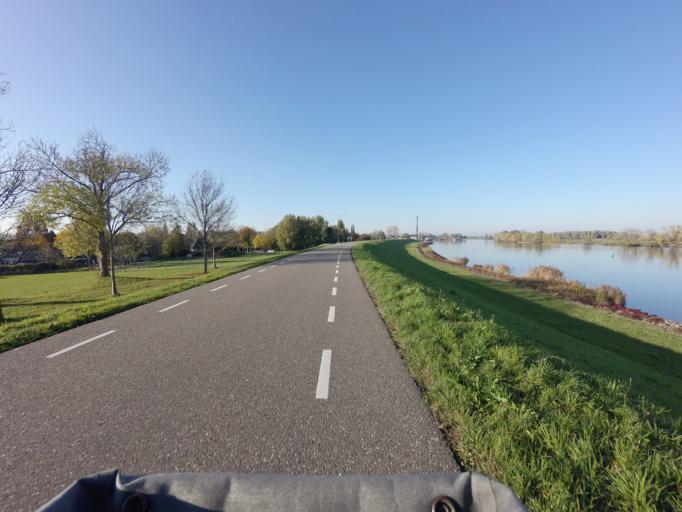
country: NL
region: North Brabant
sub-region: Gemeente Woudrichem
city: Woudrichem
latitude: 51.8068
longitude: 5.0147
